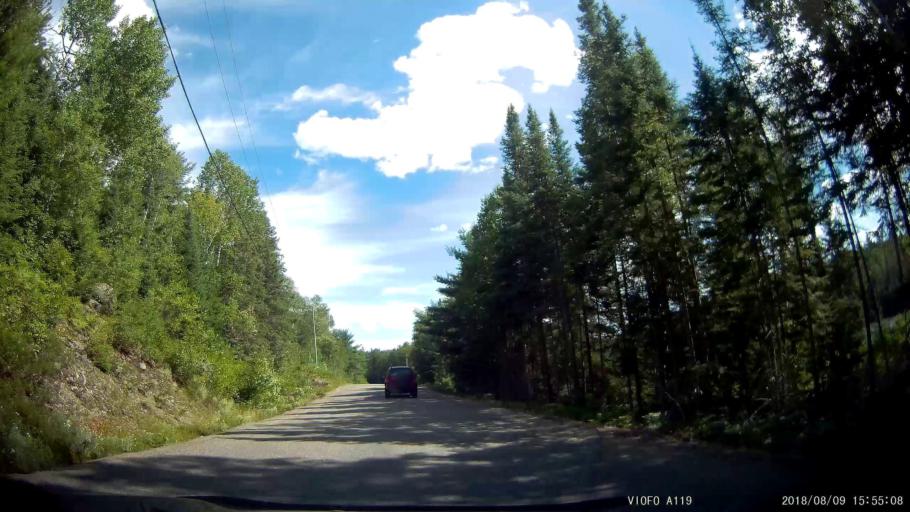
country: CA
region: Ontario
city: Rayside-Balfour
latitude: 46.6047
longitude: -81.5262
